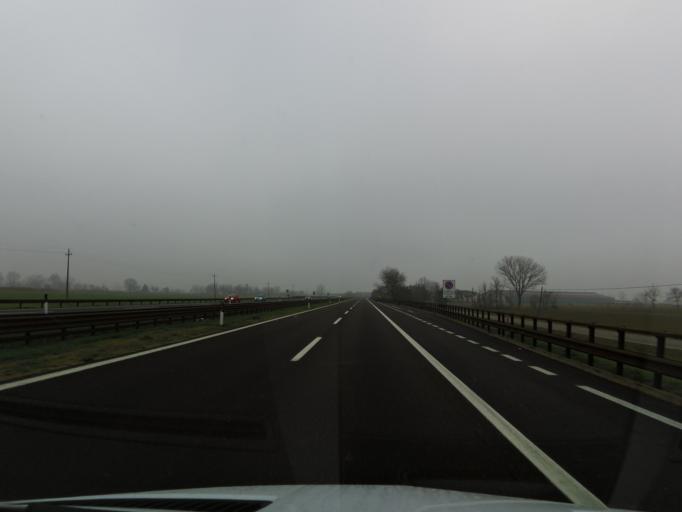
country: IT
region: Lombardy
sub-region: Provincia di Mantova
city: Bondeno
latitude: 44.9621
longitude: 10.8603
